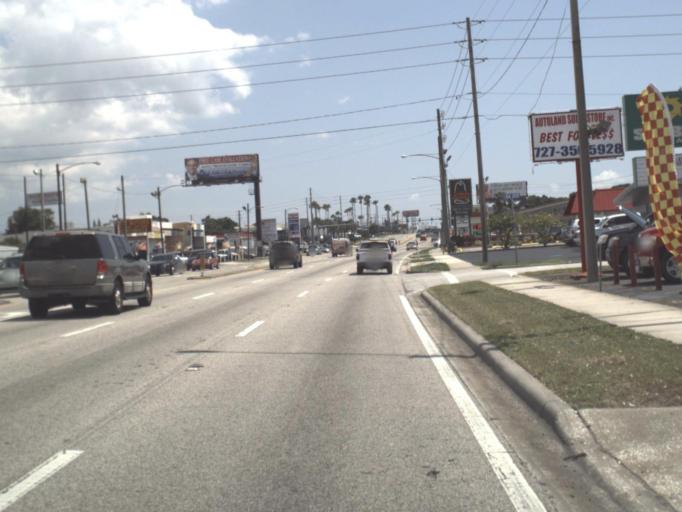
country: US
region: Florida
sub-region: Pinellas County
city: Lealman
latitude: 27.8305
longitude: -82.6798
